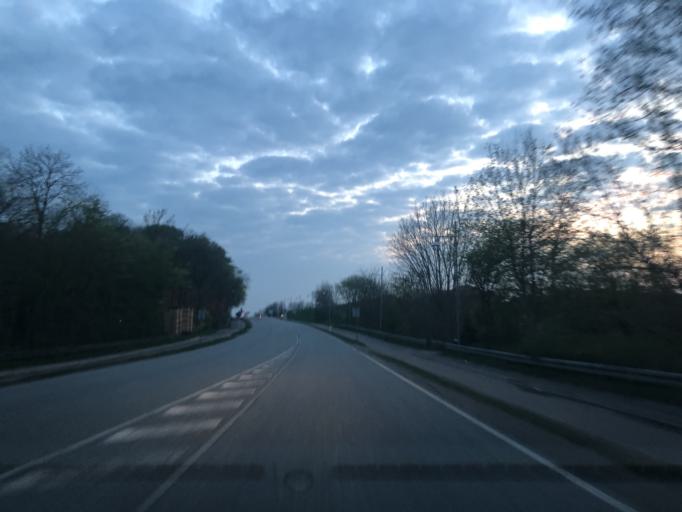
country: DK
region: Zealand
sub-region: Soro Kommune
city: Soro
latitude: 55.4419
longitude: 11.5747
